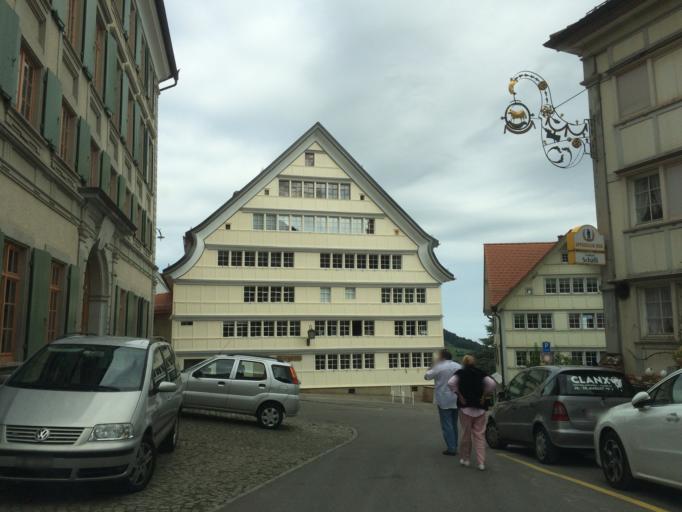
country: CH
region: Appenzell Ausserrhoden
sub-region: Bezirk Mittelland
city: Trogen
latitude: 47.4083
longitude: 9.4646
